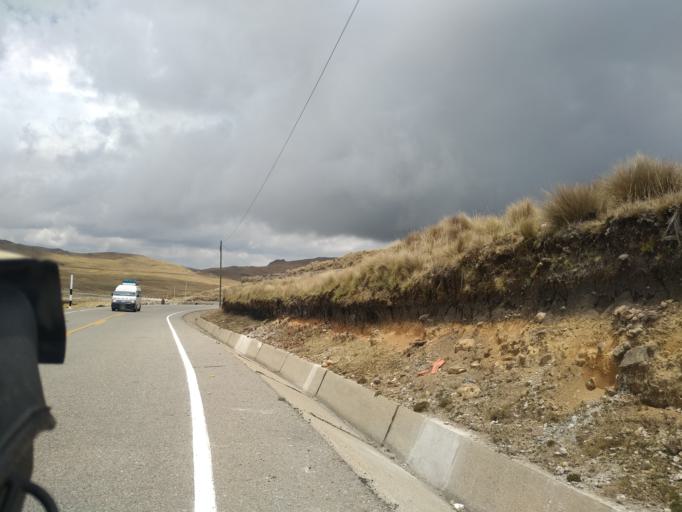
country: PE
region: La Libertad
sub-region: Provincia de Santiago de Chuco
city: Quiruvilca
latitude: -7.9419
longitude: -78.1869
